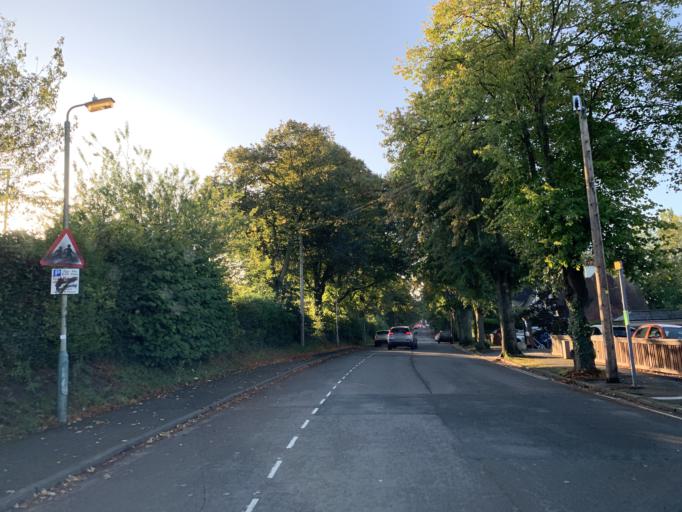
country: GB
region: England
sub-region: Wiltshire
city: Salisbury
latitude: 51.0812
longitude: -1.8001
